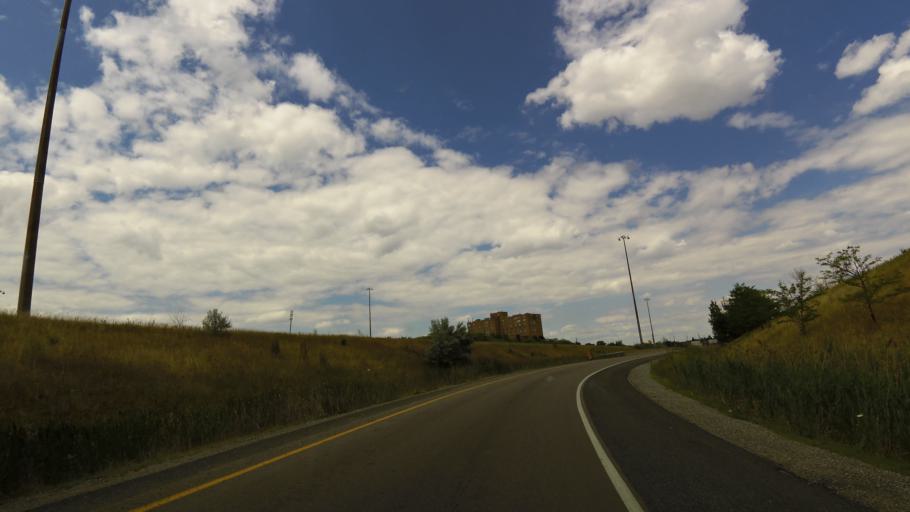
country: CA
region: Ontario
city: Mississauga
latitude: 43.5242
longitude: -79.6469
